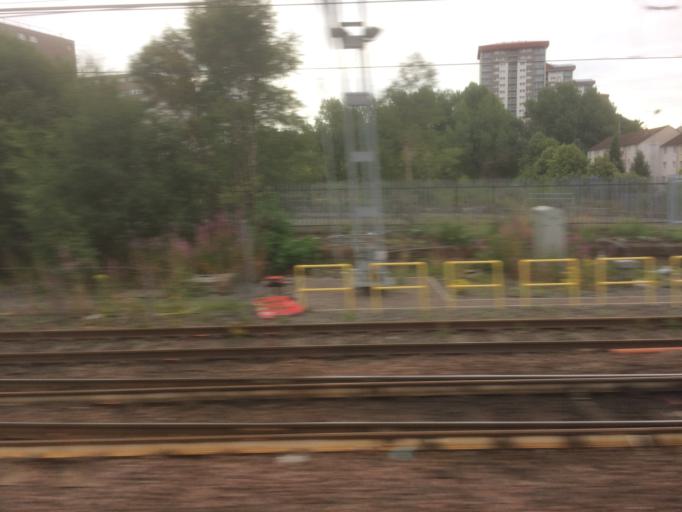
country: GB
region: Scotland
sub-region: Glasgow City
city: Glasgow
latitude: 55.8877
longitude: -4.2405
